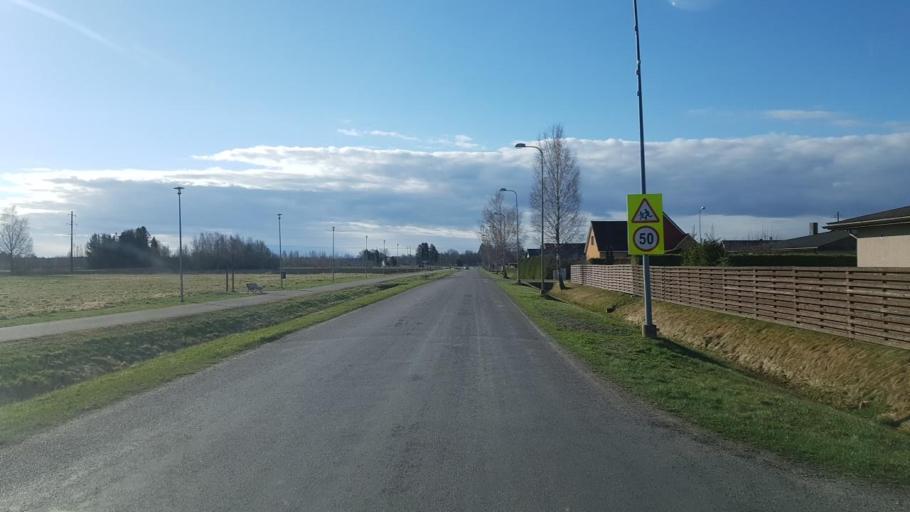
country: EE
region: Paernumaa
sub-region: Paikuse vald
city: Paikuse
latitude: 58.3923
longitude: 24.6041
